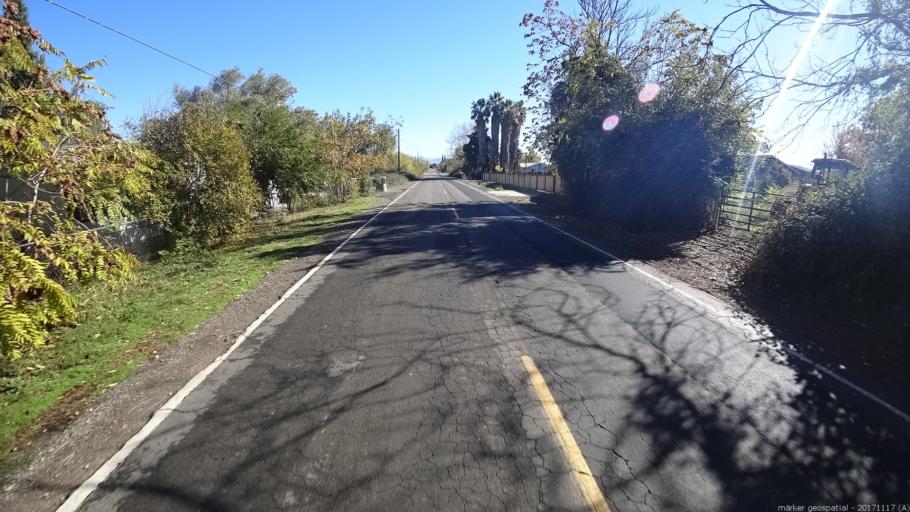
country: US
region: California
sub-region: Shasta County
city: Anderson
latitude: 40.4293
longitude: -122.2482
